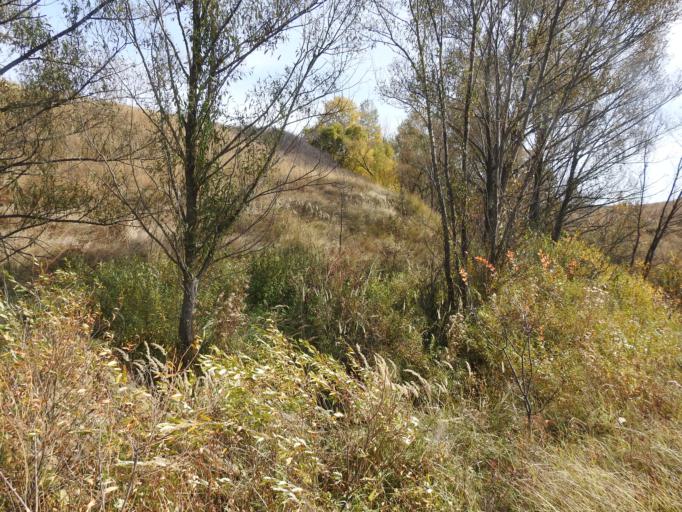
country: RU
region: Saratov
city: Baltay
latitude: 52.5409
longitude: 46.7418
